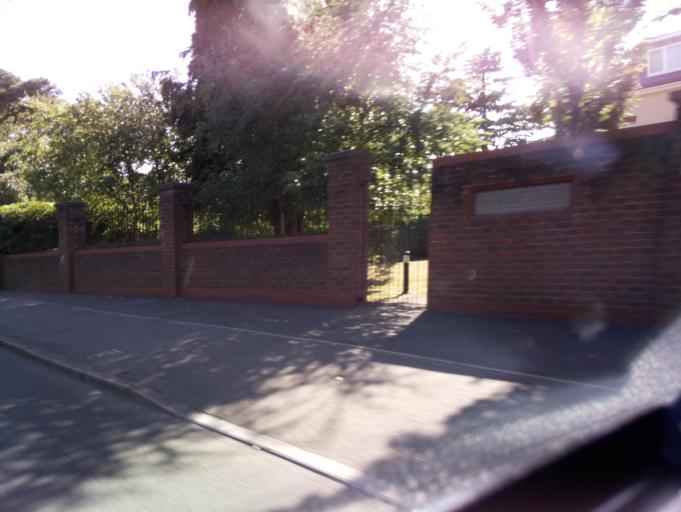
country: GB
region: England
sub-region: Dorset
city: Ferndown
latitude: 50.7957
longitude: -1.8847
